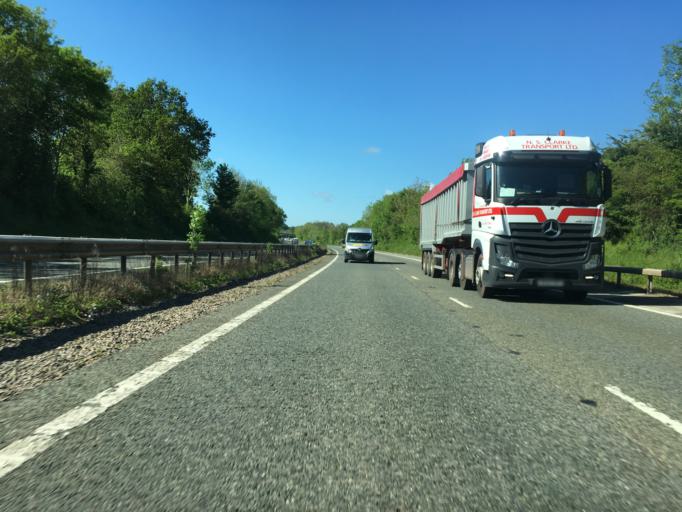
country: GB
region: England
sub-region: Herefordshire
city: Donnington
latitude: 51.9807
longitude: -2.4097
